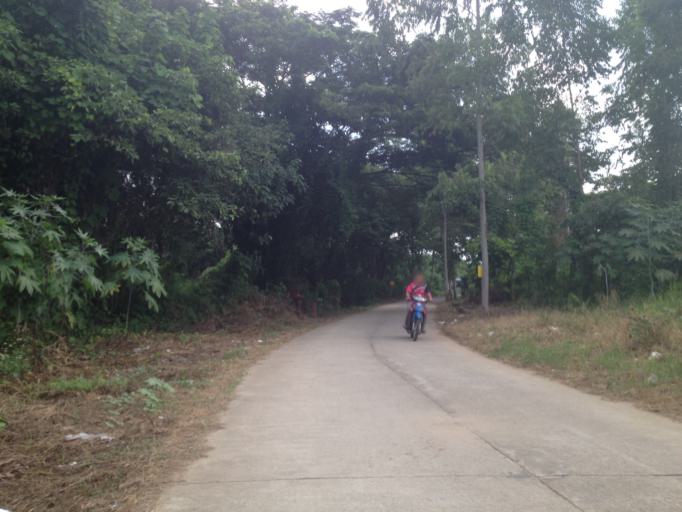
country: TH
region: Chiang Mai
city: Hang Dong
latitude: 18.7048
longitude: 98.9139
